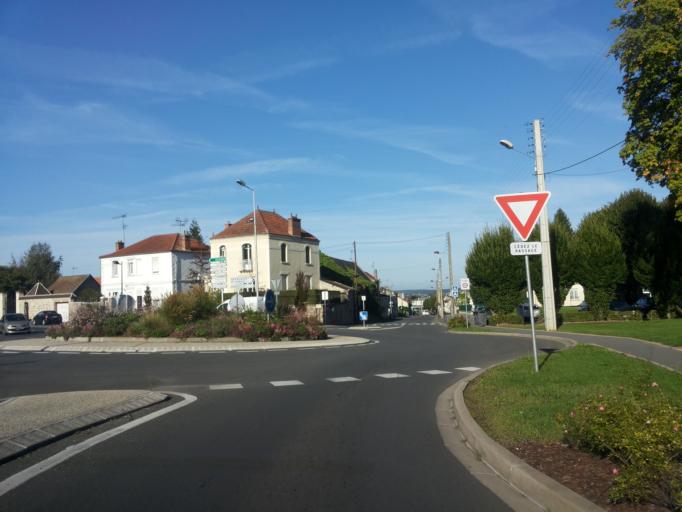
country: FR
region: Picardie
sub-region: Departement de l'Aisne
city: Laon
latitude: 49.5697
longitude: 3.6026
